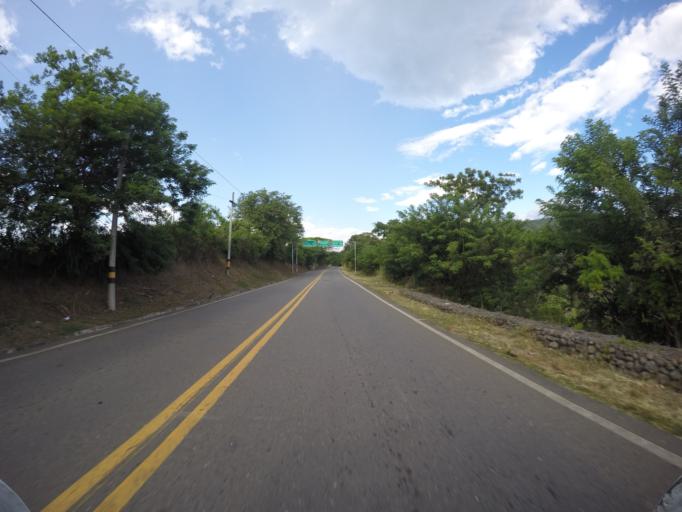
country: CO
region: Valle del Cauca
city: Cartago
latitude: 4.7250
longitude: -75.8849
